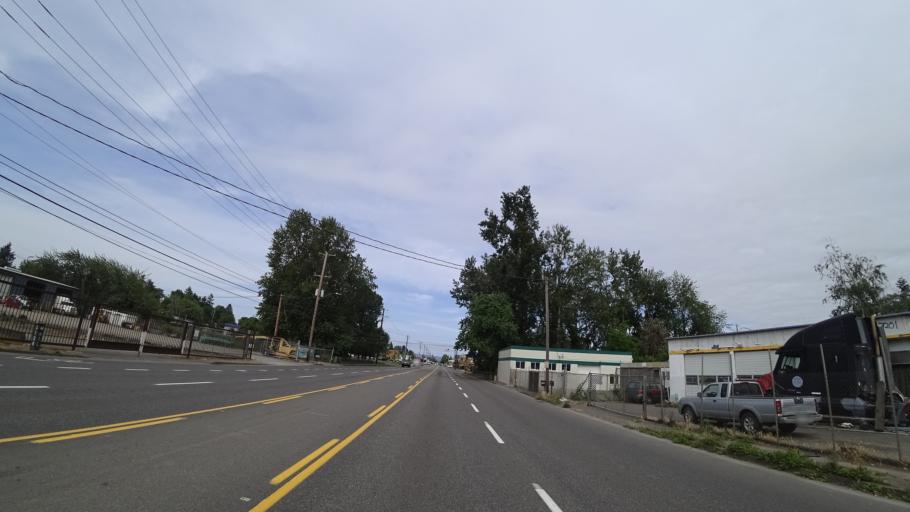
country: US
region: Oregon
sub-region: Multnomah County
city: Portland
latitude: 45.5740
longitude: -122.6324
